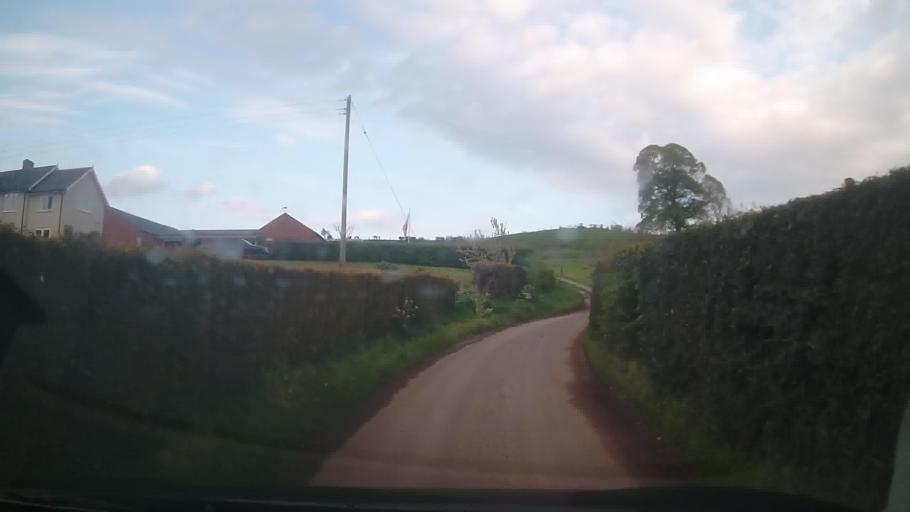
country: GB
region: England
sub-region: Shropshire
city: Ellesmere
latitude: 52.9447
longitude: -2.8684
